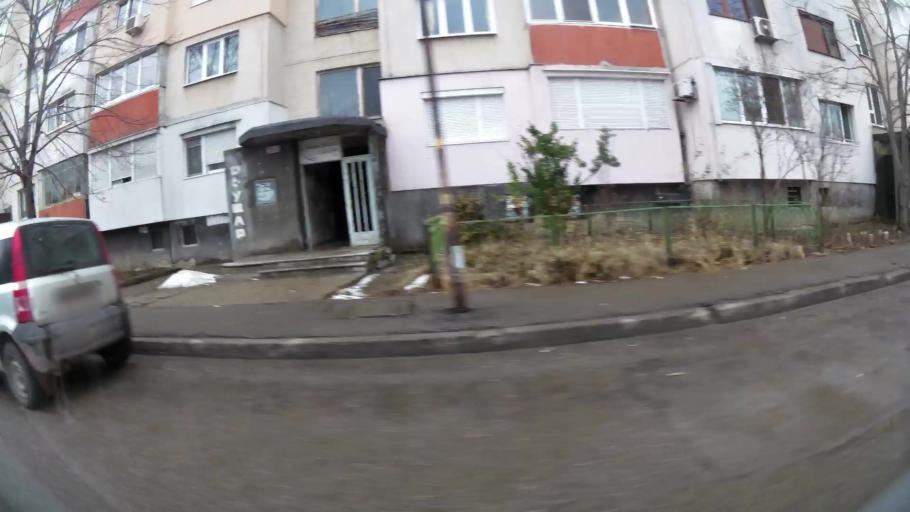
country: BG
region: Sofia-Capital
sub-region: Stolichna Obshtina
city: Sofia
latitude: 42.7395
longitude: 23.2726
